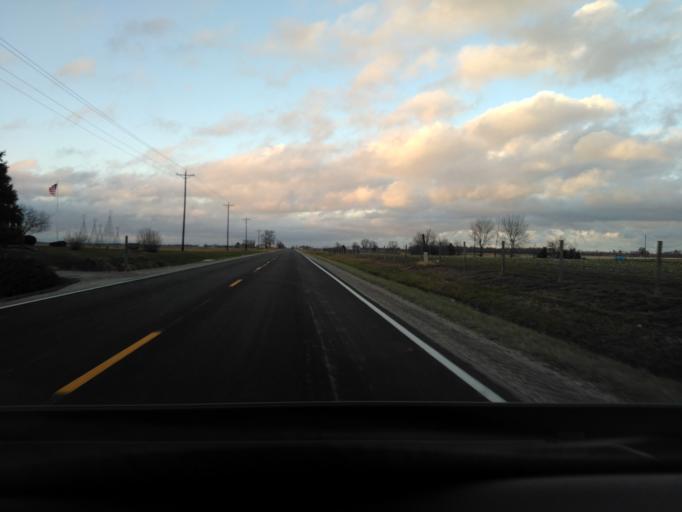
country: US
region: Illinois
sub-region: Effingham County
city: Altamont
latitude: 38.9945
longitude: -88.7487
